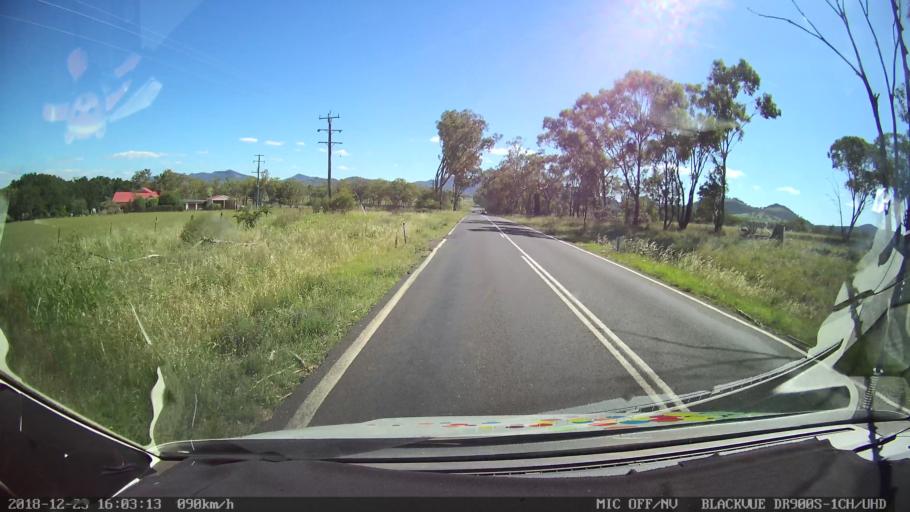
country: AU
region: New South Wales
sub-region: Tamworth Municipality
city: Phillip
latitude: -31.2410
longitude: 150.8026
